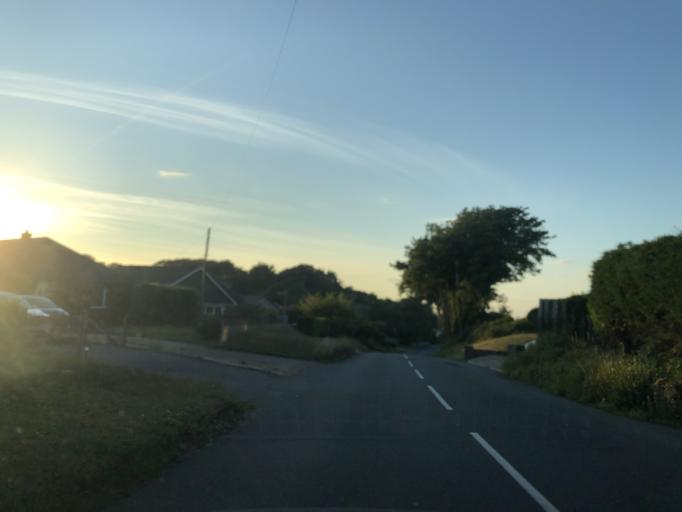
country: GB
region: England
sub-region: Isle of Wight
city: Newport
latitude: 50.6520
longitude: -1.2828
